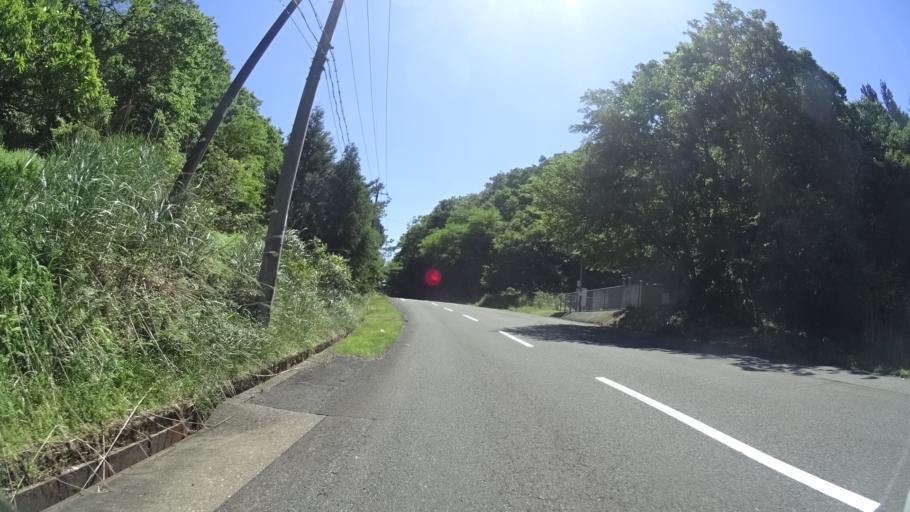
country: JP
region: Kyoto
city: Fukuchiyama
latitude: 35.4058
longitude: 135.0551
